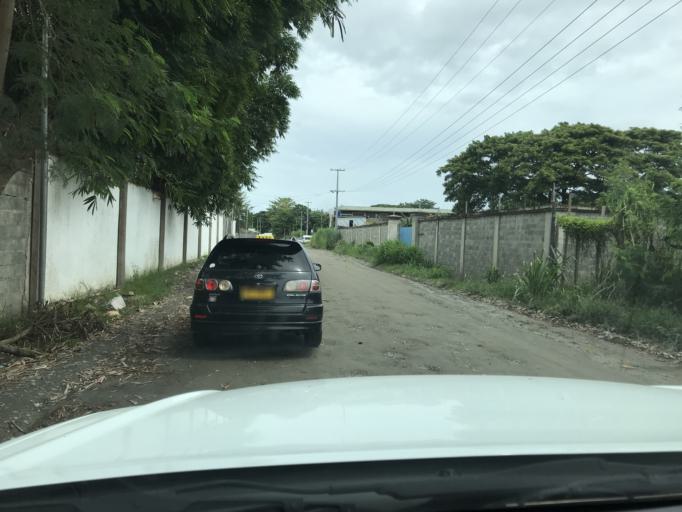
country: SB
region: Guadalcanal
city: Honiara
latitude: -9.4292
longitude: 160.0361
